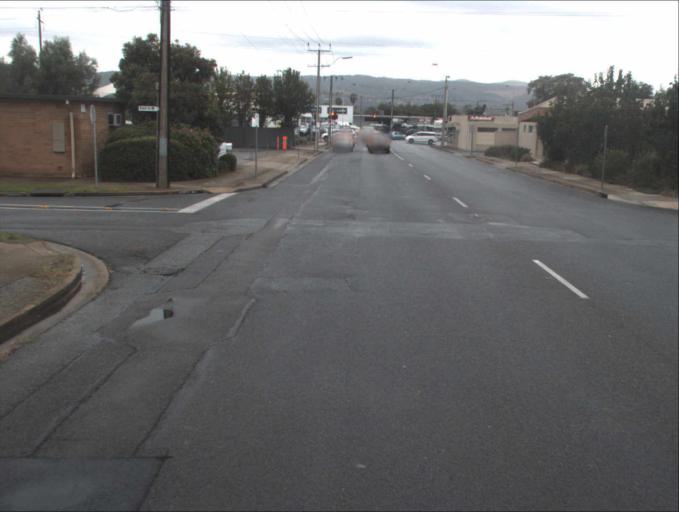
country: AU
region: South Australia
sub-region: Port Adelaide Enfield
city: Klemzig
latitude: -34.8735
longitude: 138.6319
